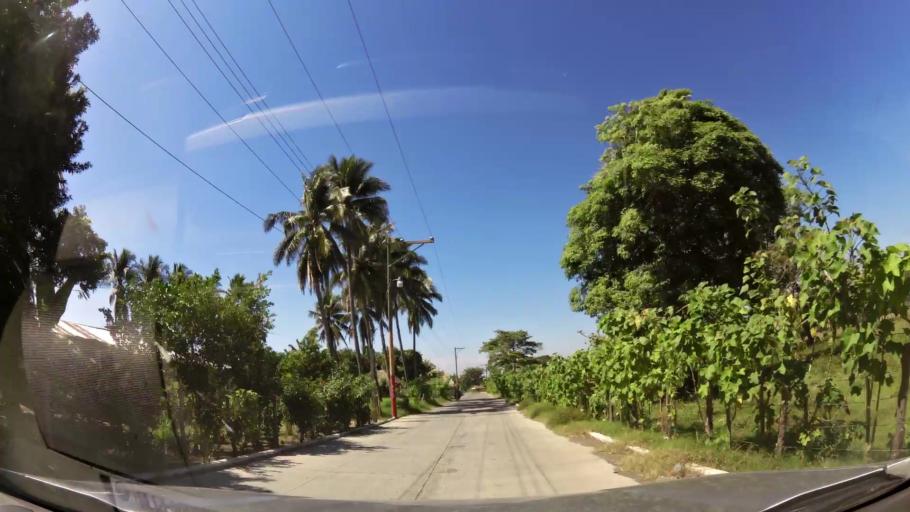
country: GT
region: Escuintla
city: Iztapa
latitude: 13.9388
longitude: -90.7037
